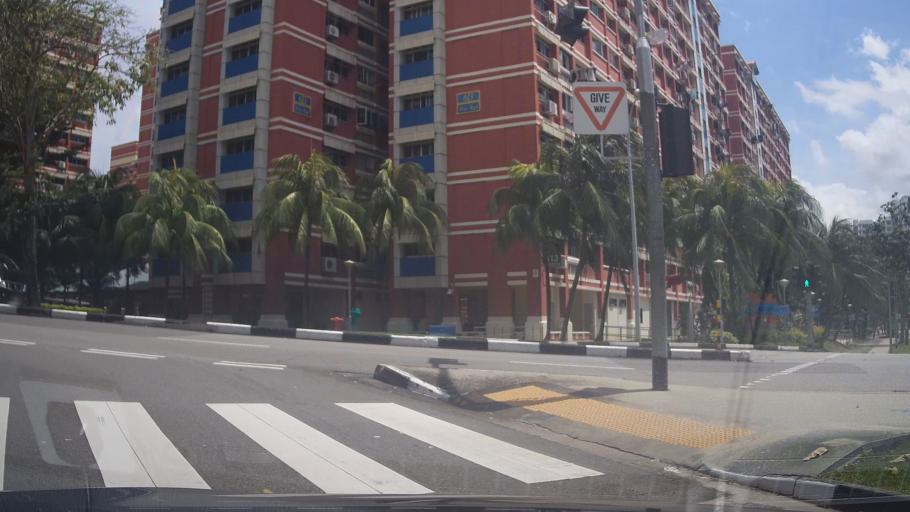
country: MY
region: Johor
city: Kampung Pasir Gudang Baru
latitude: 1.3752
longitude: 103.9408
